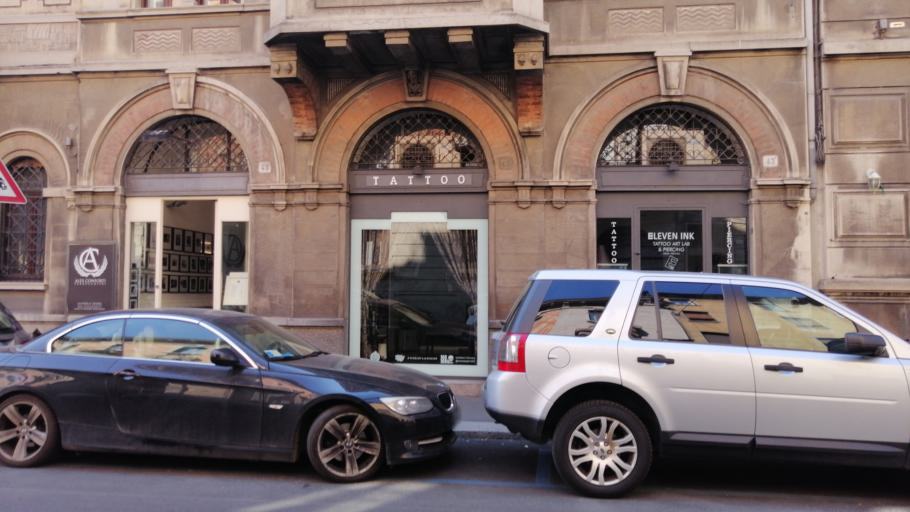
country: IT
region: Emilia-Romagna
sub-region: Provincia di Piacenza
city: Piacenza
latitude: 45.0541
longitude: 9.6956
